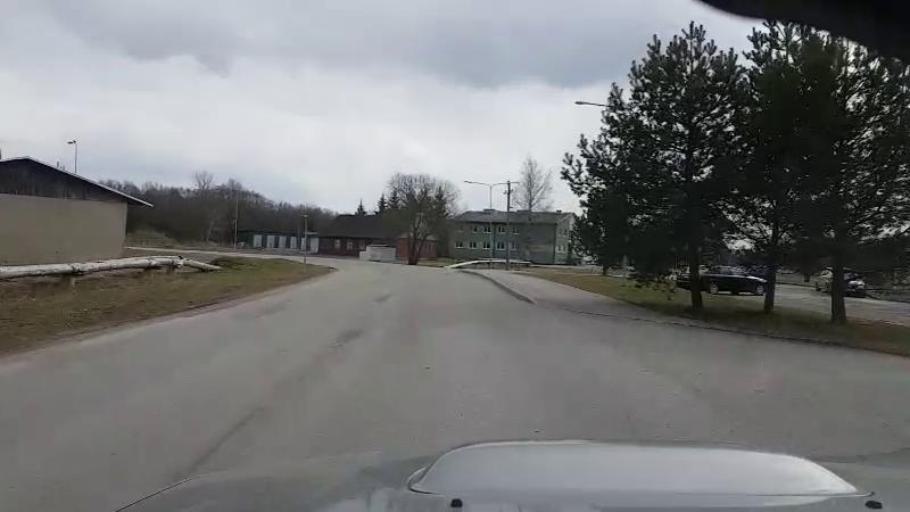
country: EE
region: Jaervamaa
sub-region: Paide linn
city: Paide
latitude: 58.8822
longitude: 25.5509
